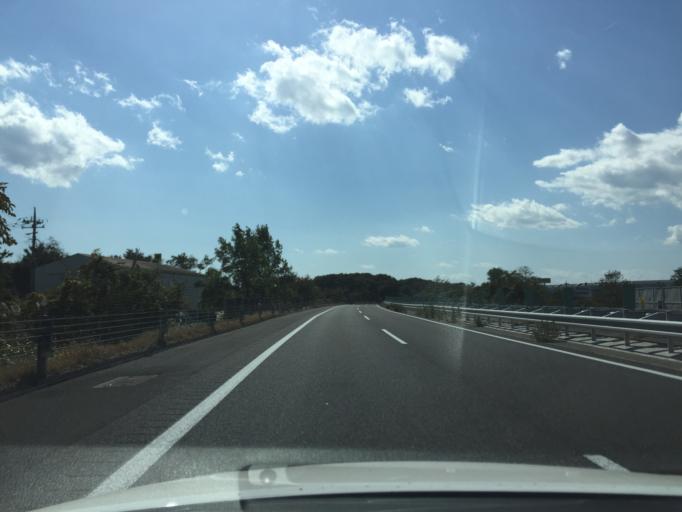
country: JP
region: Fukushima
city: Sukagawa
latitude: 37.2694
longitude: 140.3495
